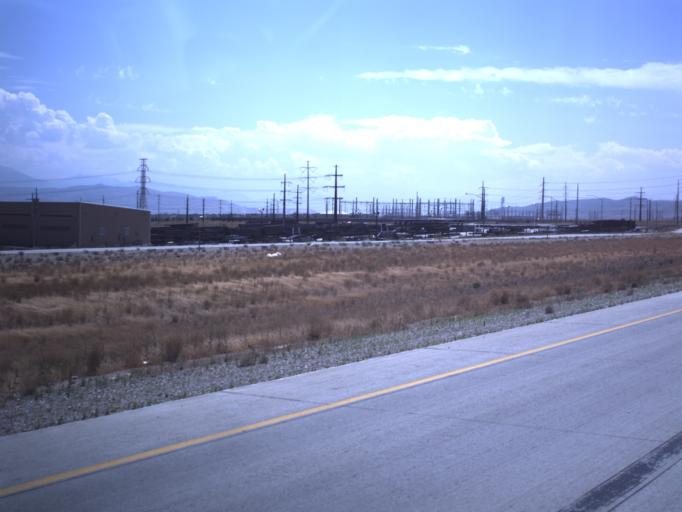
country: US
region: Utah
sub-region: Salt Lake County
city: Oquirrh
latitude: 40.5745
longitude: -112.0345
